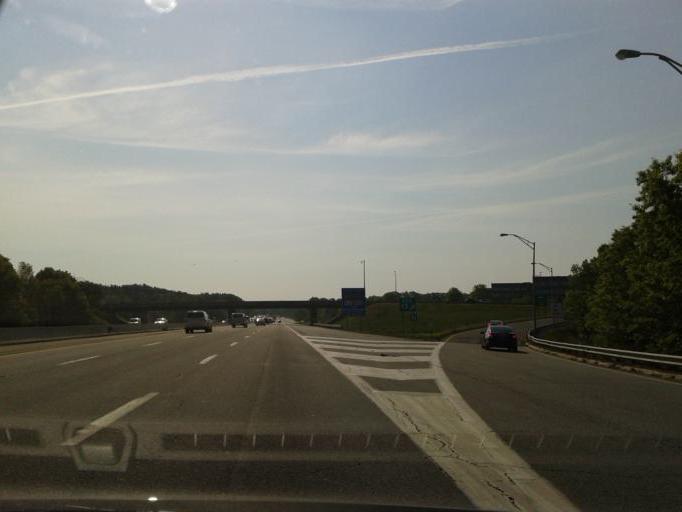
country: US
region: Massachusetts
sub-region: Middlesex County
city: Cochituate
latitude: 42.3131
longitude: -71.3873
